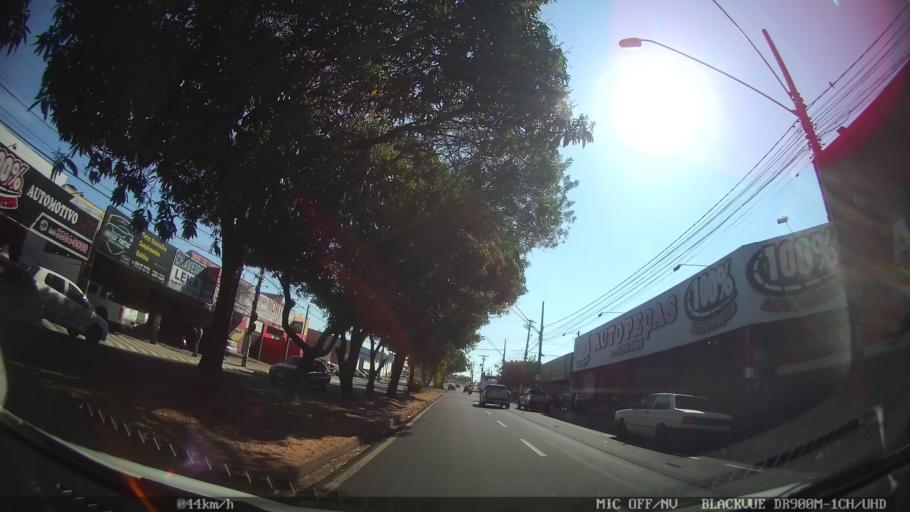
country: BR
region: Sao Paulo
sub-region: Sao Jose Do Rio Preto
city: Sao Jose do Rio Preto
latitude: -20.7729
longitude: -49.3854
